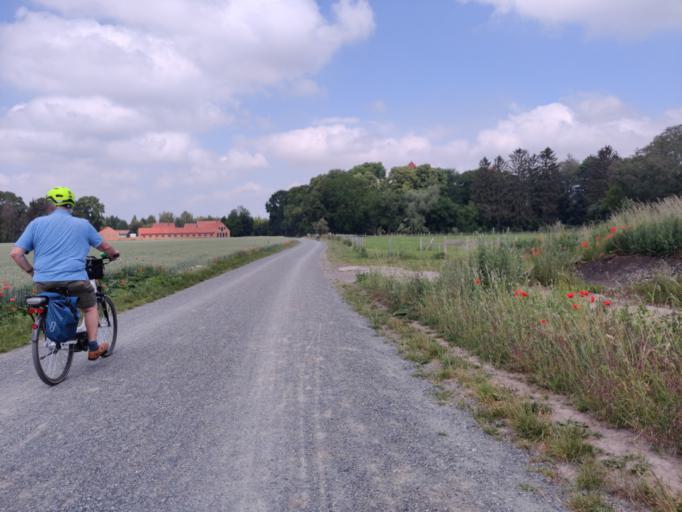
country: DE
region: Lower Saxony
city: Hildesheim
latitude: 52.1122
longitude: 9.9839
